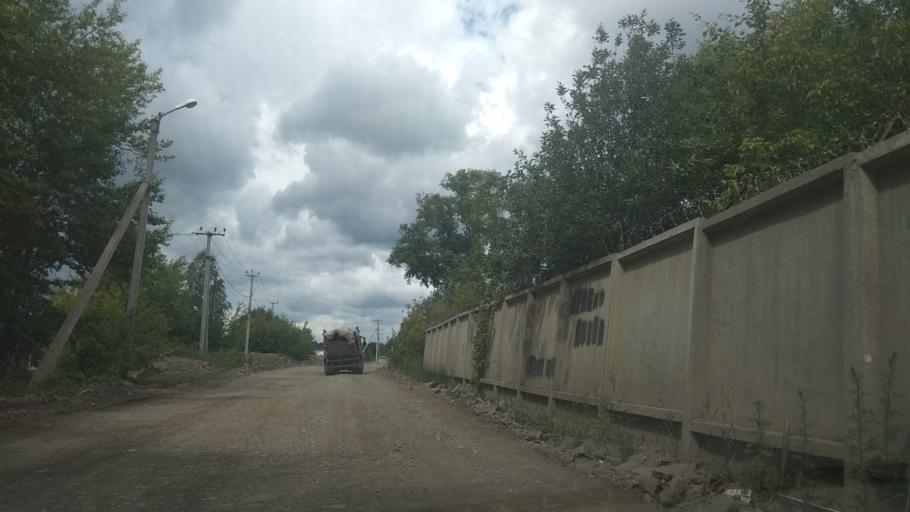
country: RU
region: Sverdlovsk
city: Verkhnyaya Pyshma
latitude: 56.9164
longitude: 60.5751
